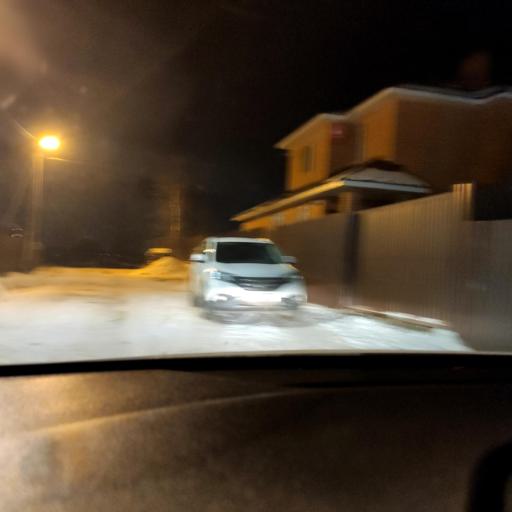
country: RU
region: Tatarstan
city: Stolbishchi
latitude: 55.7534
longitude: 49.2703
